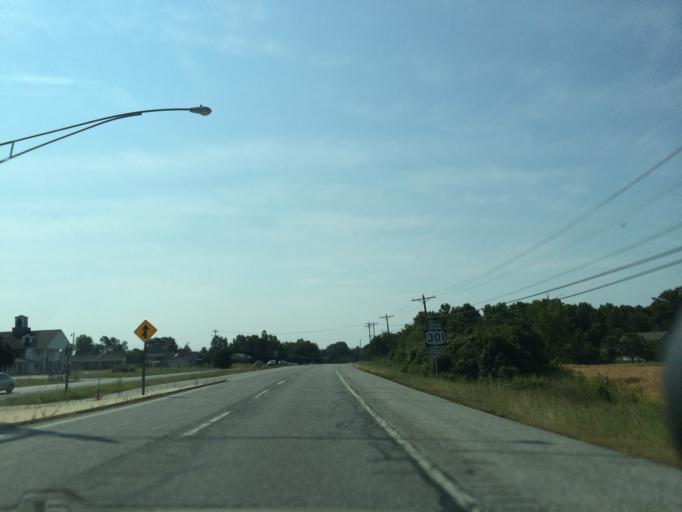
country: US
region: Maryland
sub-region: Charles County
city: La Plata
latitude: 38.4076
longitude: -76.9537
